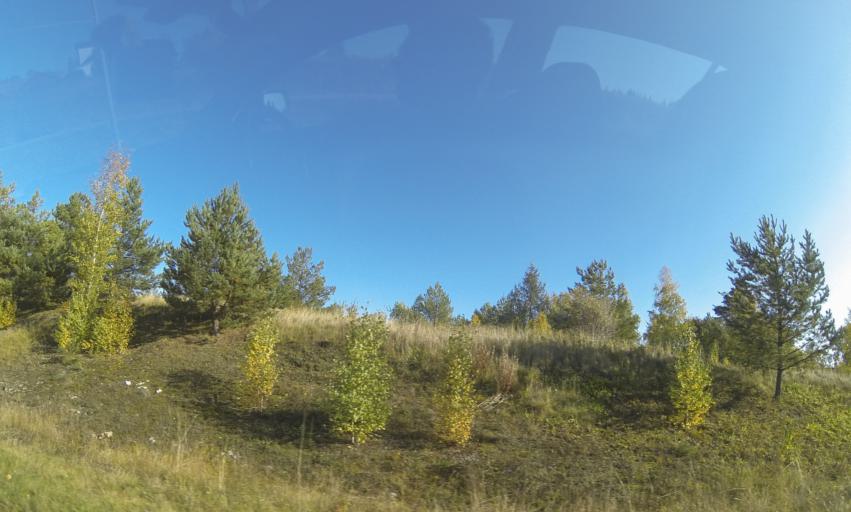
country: SE
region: Vaestmanland
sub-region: Vasteras
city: Skultuna
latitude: 59.5737
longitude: 16.3985
